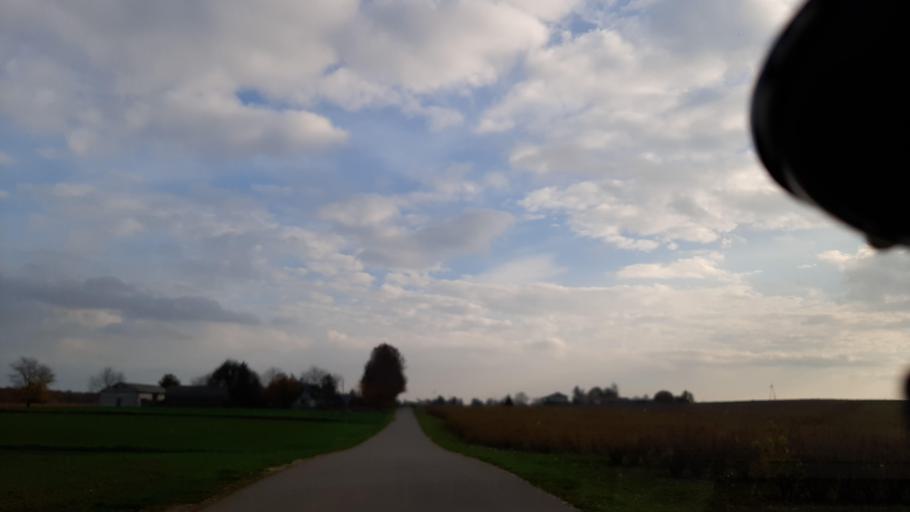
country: PL
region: Lublin Voivodeship
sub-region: Powiat pulawski
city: Markuszow
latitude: 51.3354
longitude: 22.2764
